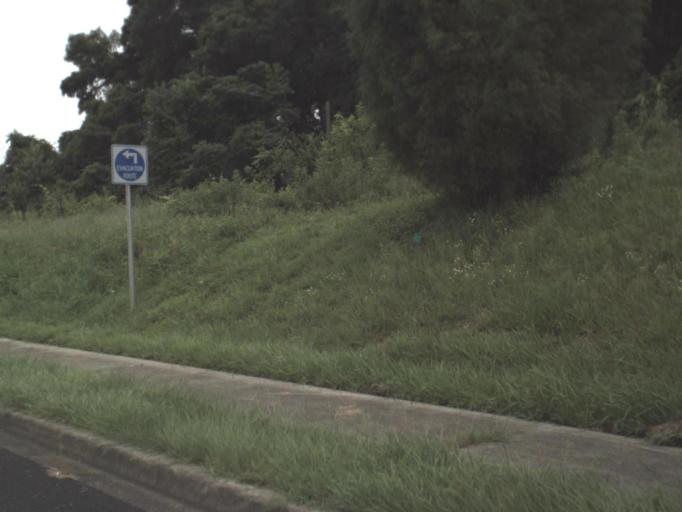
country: US
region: Florida
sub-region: Citrus County
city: Lecanto
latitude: 28.8517
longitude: -82.4888
